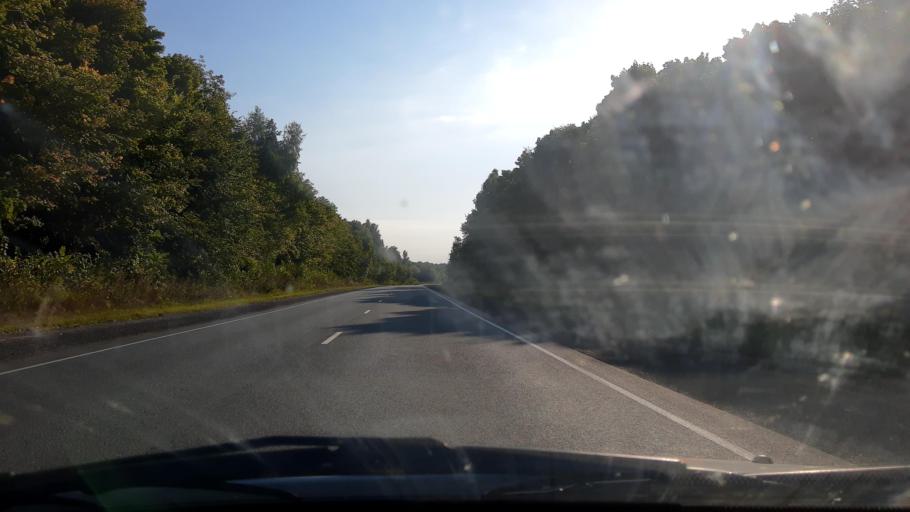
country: RU
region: Bashkortostan
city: Oktyabr'skiy
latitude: 54.4441
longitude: 53.5458
